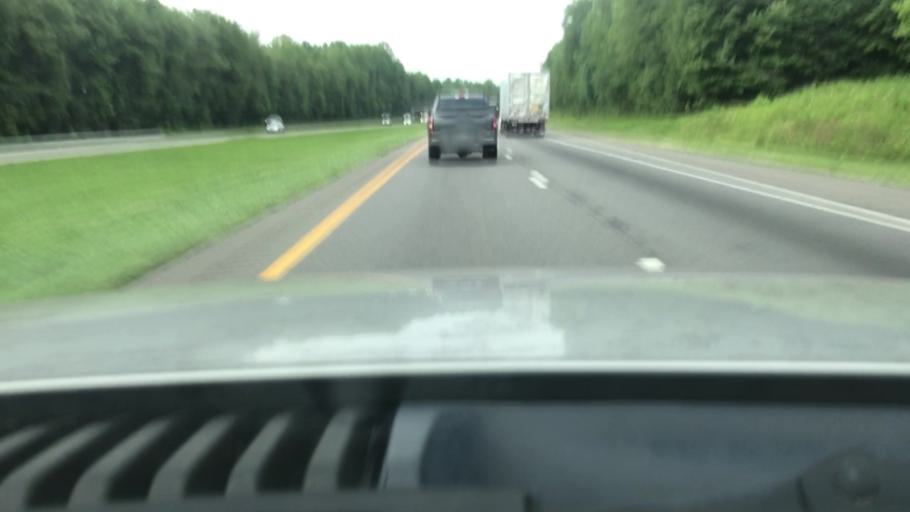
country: US
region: North Carolina
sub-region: Surry County
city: Dobson
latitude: 36.3600
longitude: -80.7984
